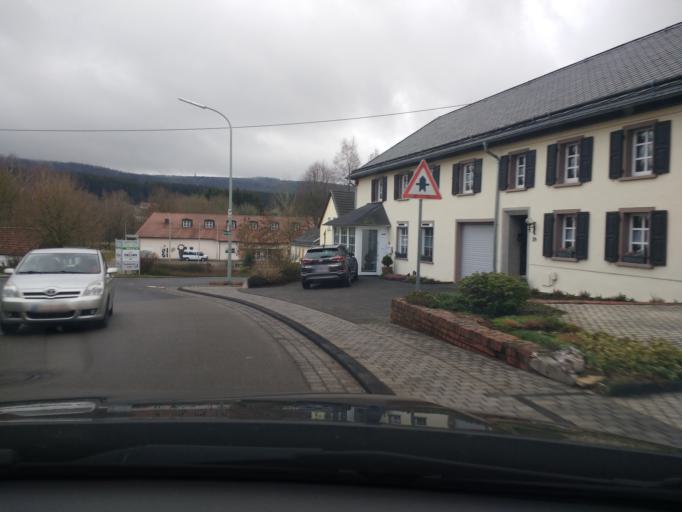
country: DE
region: Rheinland-Pfalz
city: Waldweiler
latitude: 49.6127
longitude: 6.7988
